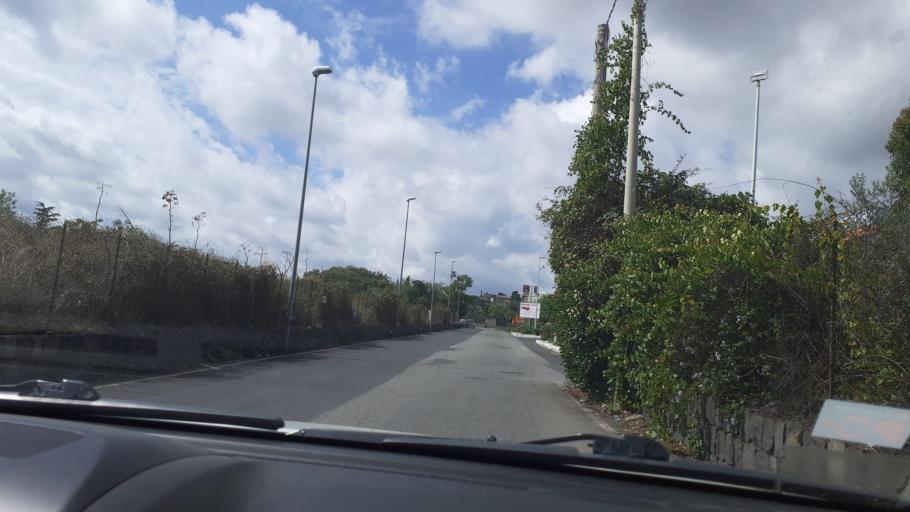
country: IT
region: Sicily
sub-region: Catania
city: San Giovanni la Punta
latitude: 37.5891
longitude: 15.0926
